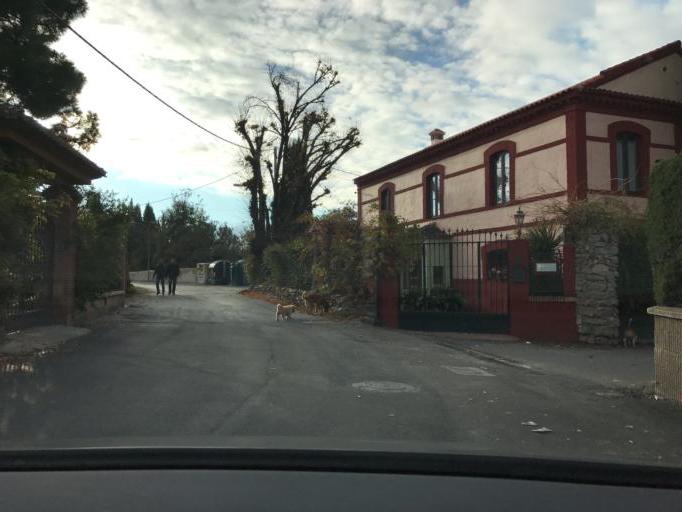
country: ES
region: Andalusia
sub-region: Provincia de Granada
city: Huetor Vega
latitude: 37.1417
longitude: -3.5728
